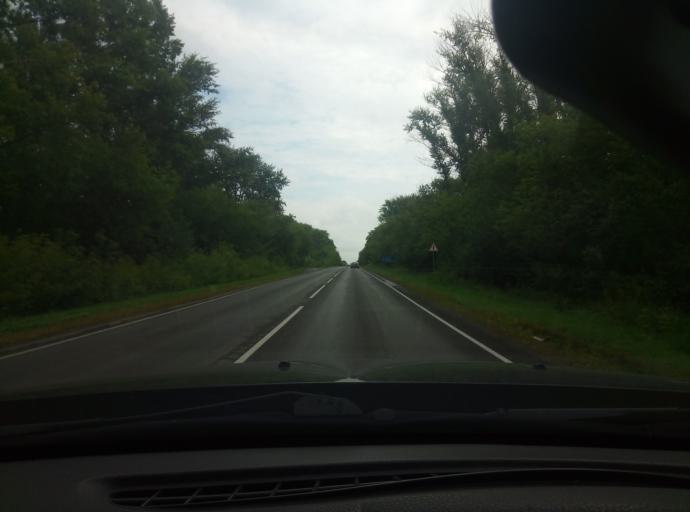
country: RU
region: Tula
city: Kimovsk
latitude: 53.9709
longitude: 38.4776
